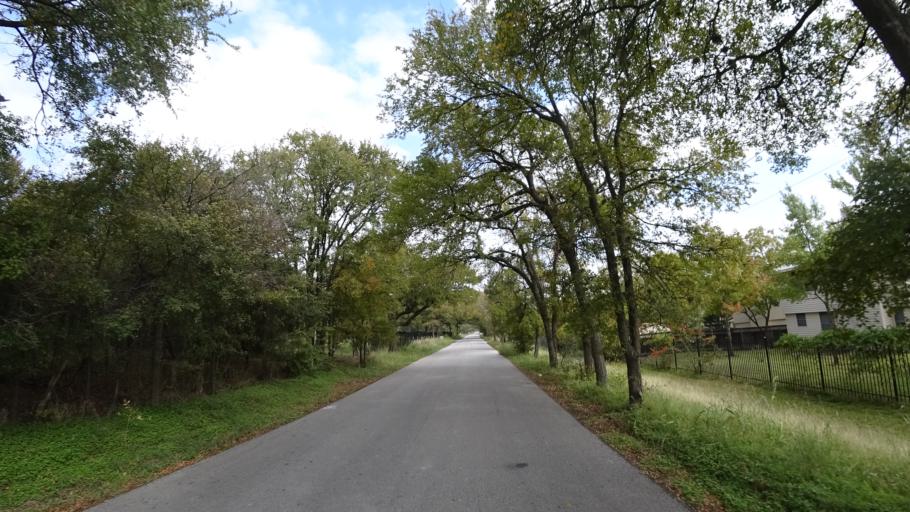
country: US
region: Texas
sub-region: Travis County
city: Shady Hollow
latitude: 30.1933
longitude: -97.8372
